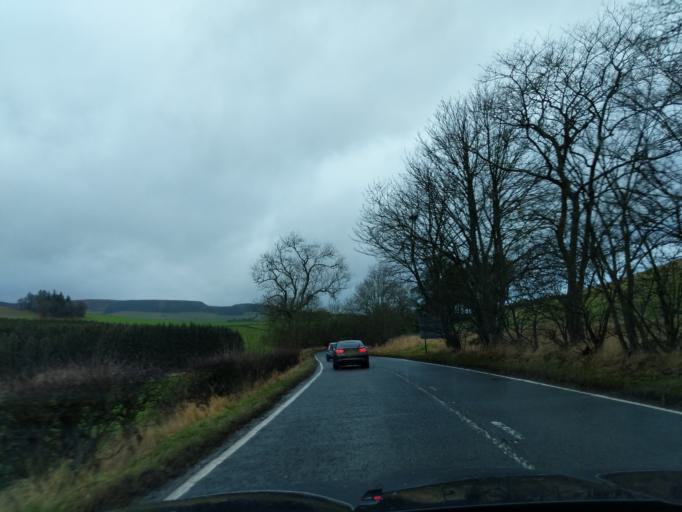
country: GB
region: Scotland
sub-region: The Scottish Borders
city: Galashiels
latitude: 55.6544
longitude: -2.8670
